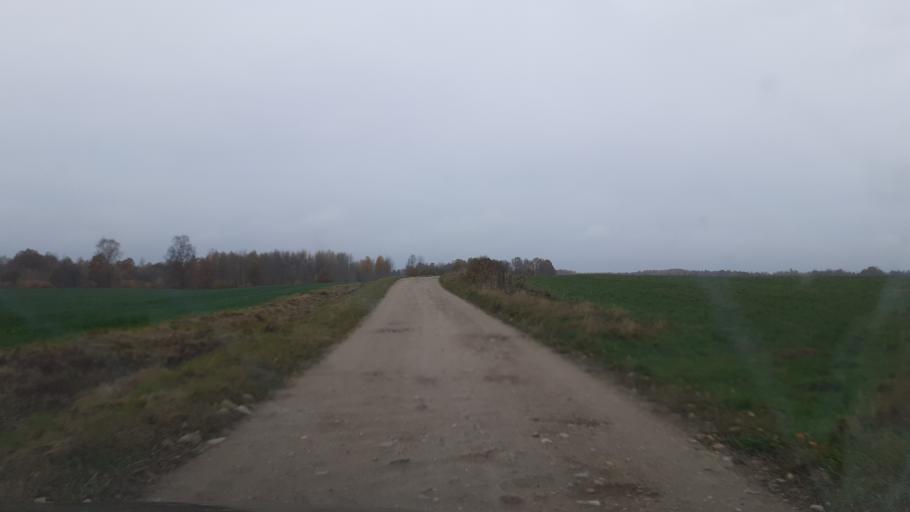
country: LV
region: Saldus Rajons
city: Saldus
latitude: 56.8657
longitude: 22.3460
